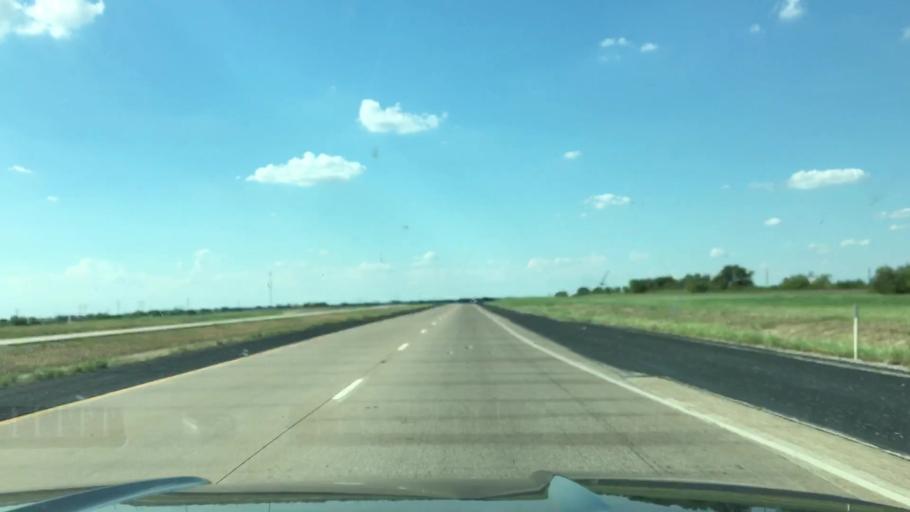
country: US
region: Texas
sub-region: Wise County
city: New Fairview
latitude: 33.1080
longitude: -97.4751
